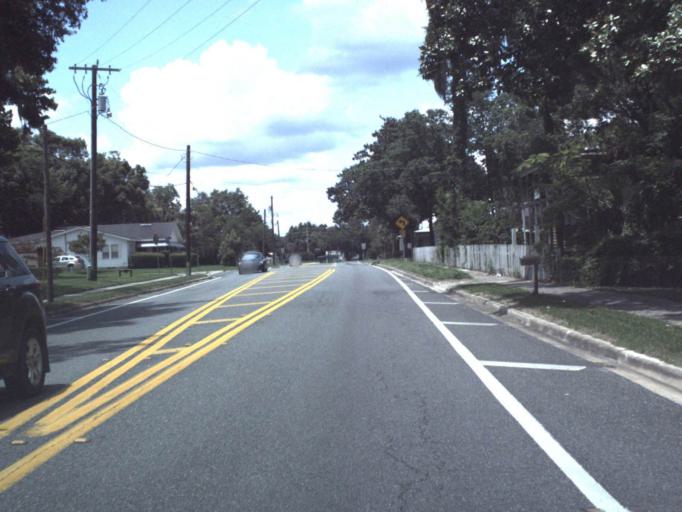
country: US
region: Florida
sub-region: Bradford County
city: Starke
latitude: 29.9403
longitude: -82.1063
